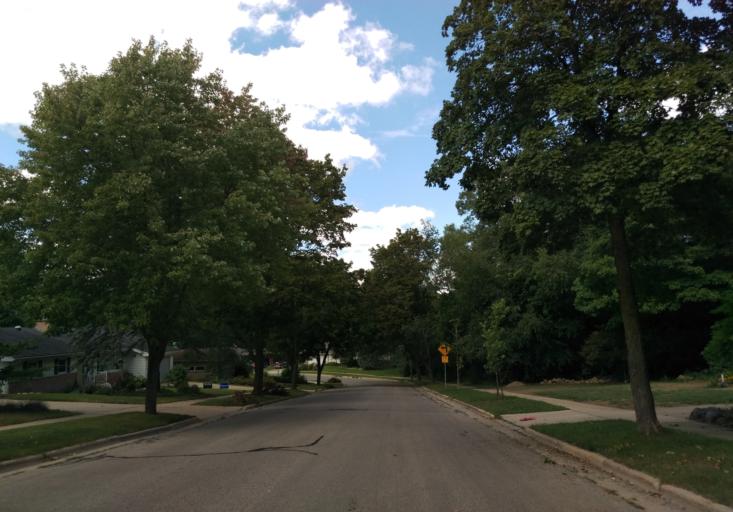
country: US
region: Wisconsin
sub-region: Dane County
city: Middleton
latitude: 43.0666
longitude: -89.4828
